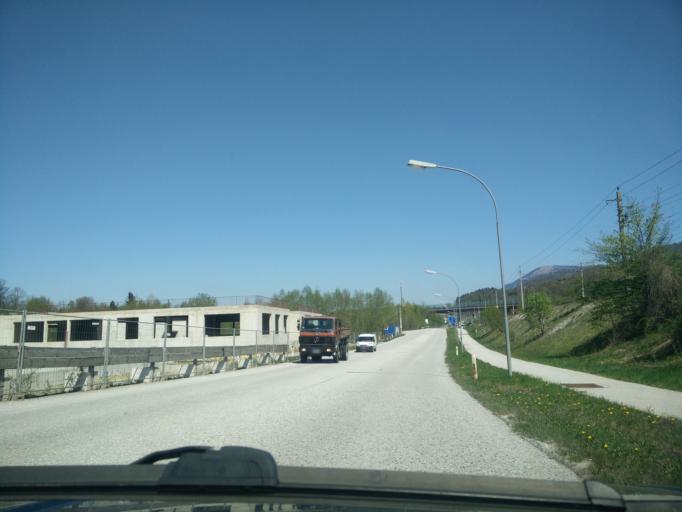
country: AT
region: Salzburg
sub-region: Politischer Bezirk Hallein
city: Puch bei Hallein
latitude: 47.7264
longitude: 13.0875
